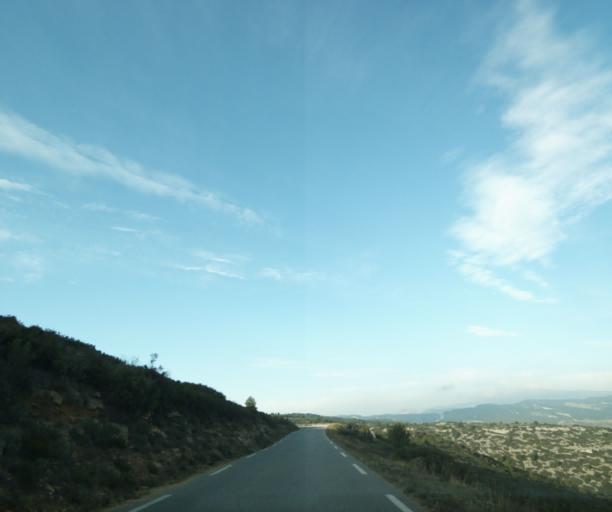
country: FR
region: Provence-Alpes-Cote d'Azur
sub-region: Departement des Bouches-du-Rhone
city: Cassis
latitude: 43.1910
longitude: 5.5590
